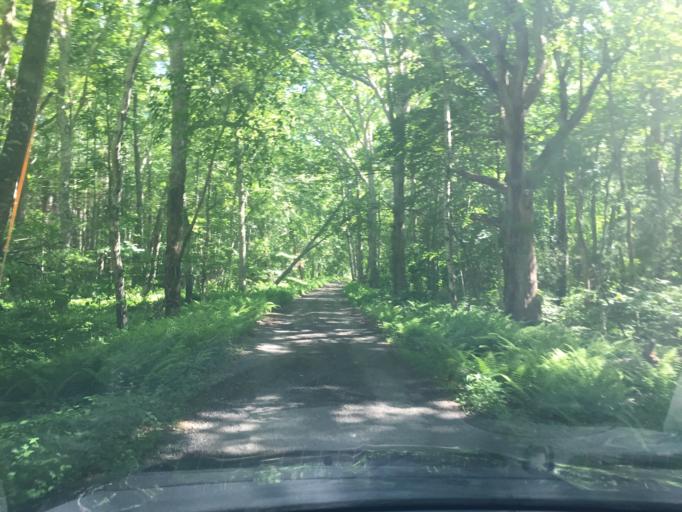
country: US
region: Rhode Island
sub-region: Washington County
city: Hopkinton
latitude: 41.5163
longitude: -71.8009
